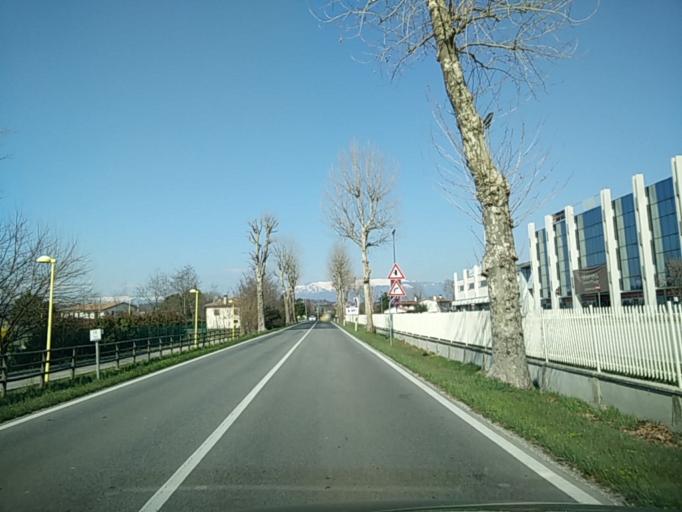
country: IT
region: Veneto
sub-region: Provincia di Treviso
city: Nervesa della Battaglia
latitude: 45.8165
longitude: 12.2266
